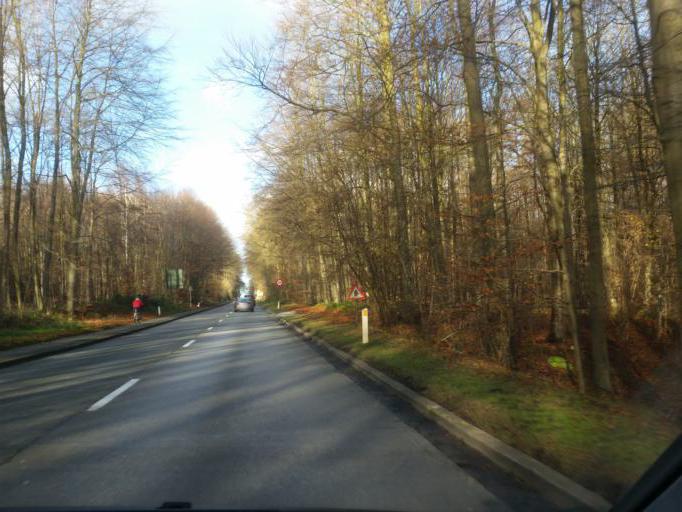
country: BE
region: Flanders
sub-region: Provincie Vlaams-Brabant
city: Hoeilaart
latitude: 50.7745
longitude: 4.4365
